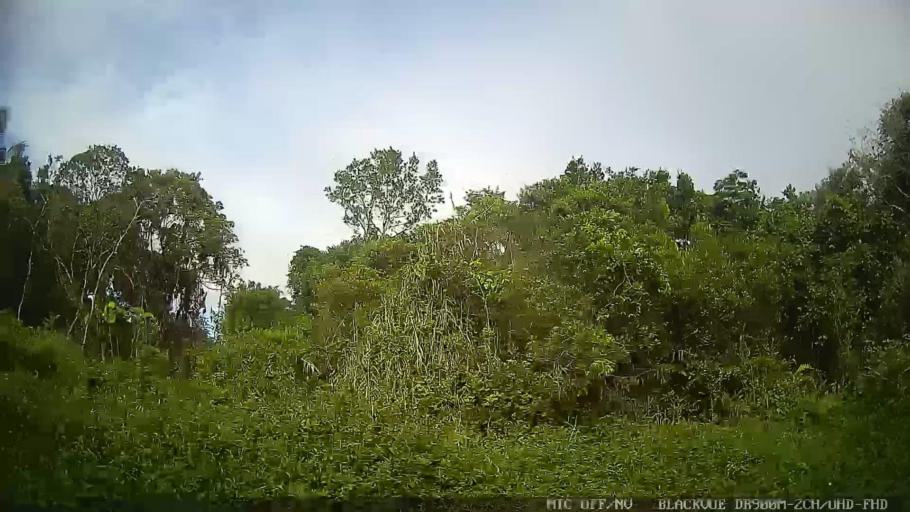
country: BR
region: Sao Paulo
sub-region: Peruibe
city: Peruibe
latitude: -24.2353
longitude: -46.9078
